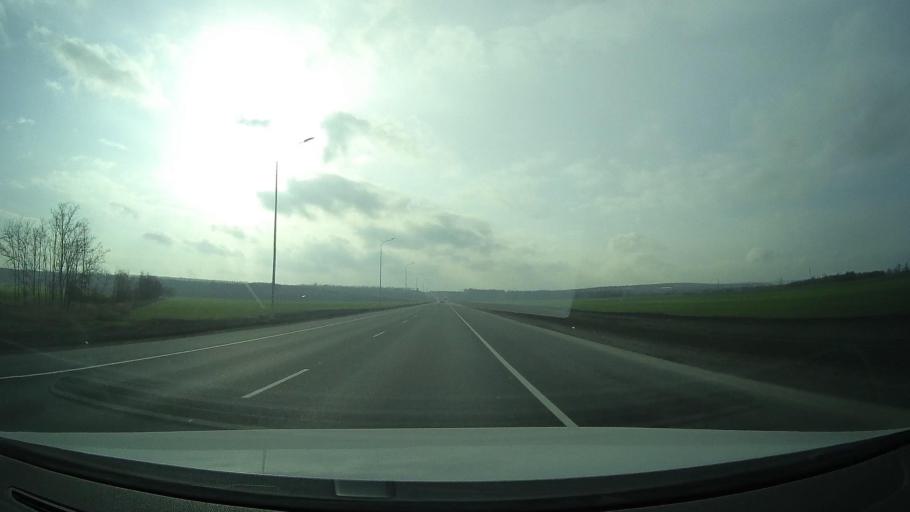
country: RU
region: Rostov
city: Grushevskaya
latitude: 47.4449
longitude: 39.8767
